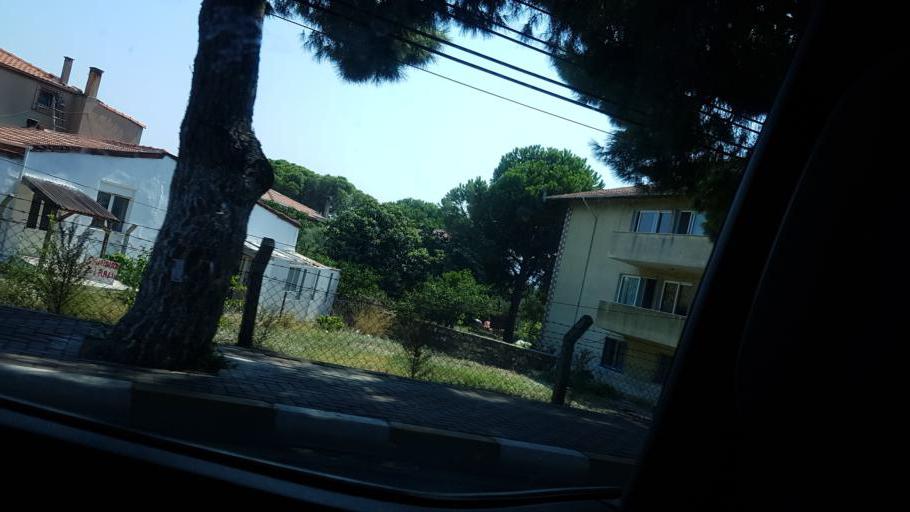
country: TR
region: Izmir
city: Urla
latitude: 38.3605
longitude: 26.7717
